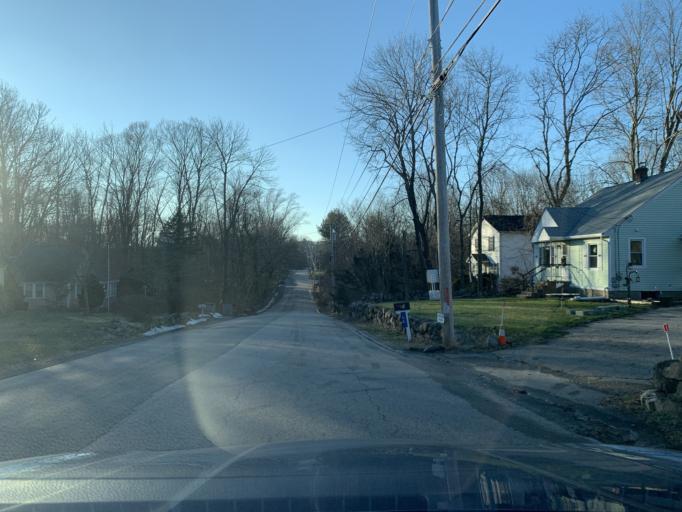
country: US
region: Rhode Island
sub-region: Kent County
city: West Warwick
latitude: 41.7385
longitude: -71.5501
